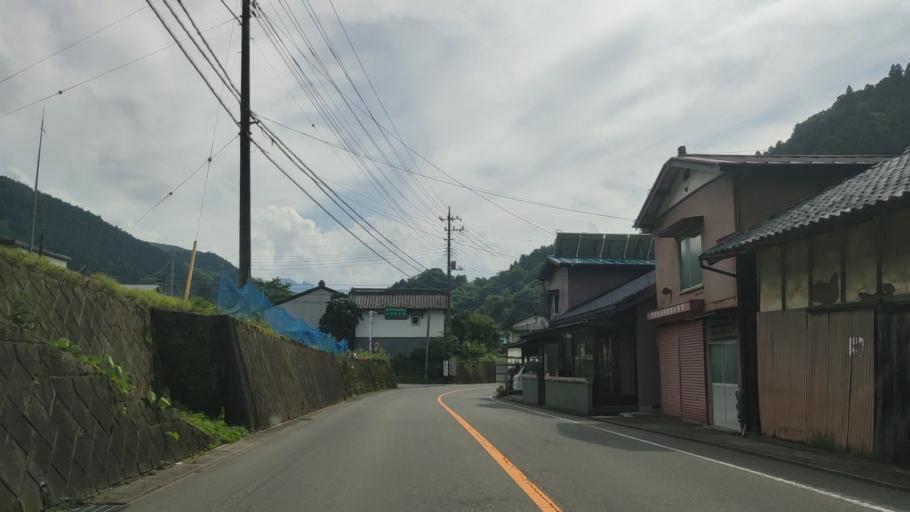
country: JP
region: Gunma
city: Tomioka
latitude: 36.1846
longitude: 138.7470
